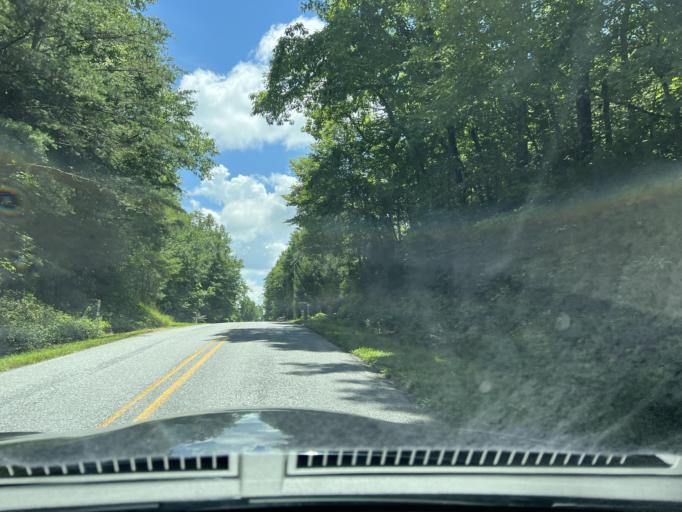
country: US
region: North Carolina
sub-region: Henderson County
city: Fruitland
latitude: 35.4174
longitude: -82.4026
